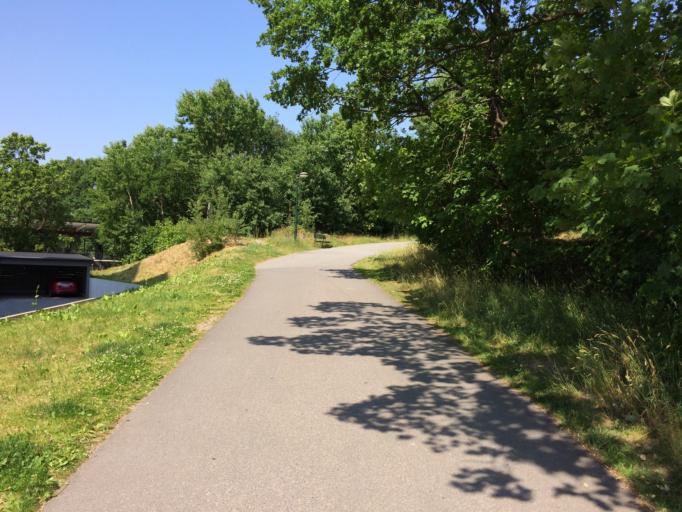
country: SE
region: Stockholm
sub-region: Huddinge Kommun
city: Segeltorp
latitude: 59.2946
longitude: 17.9790
